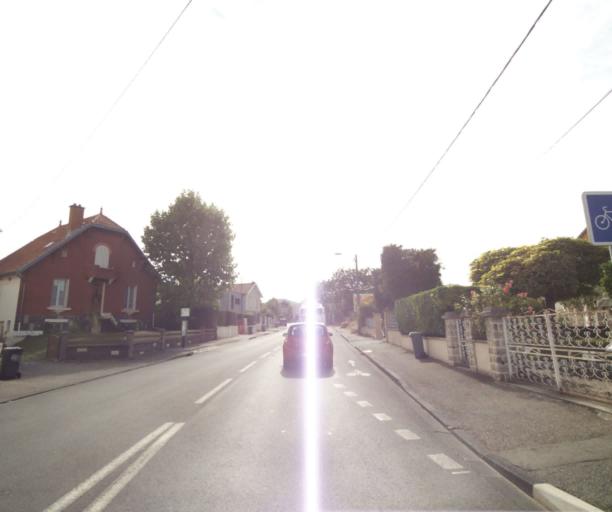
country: FR
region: Auvergne
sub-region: Departement du Puy-de-Dome
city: Aubiere
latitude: 45.7460
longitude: 3.1092
